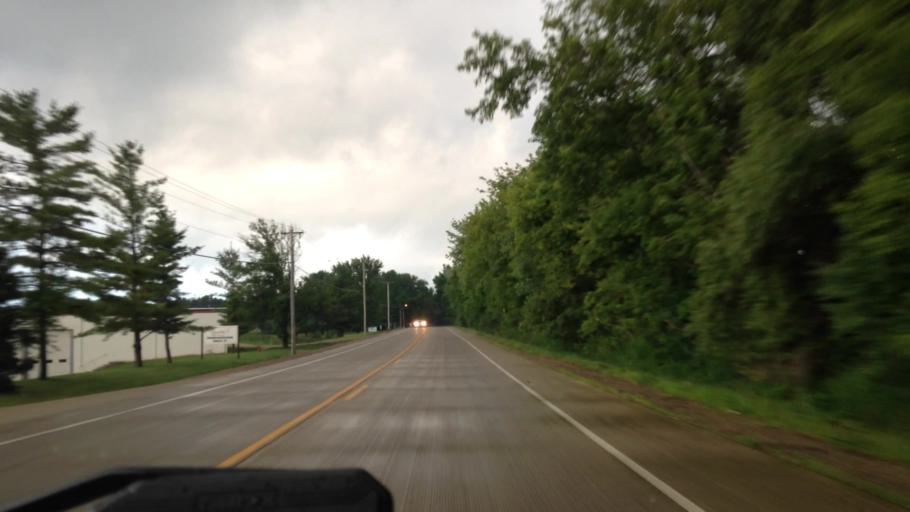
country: US
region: Wisconsin
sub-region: Dodge County
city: Mayville
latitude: 43.4842
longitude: -88.5519
